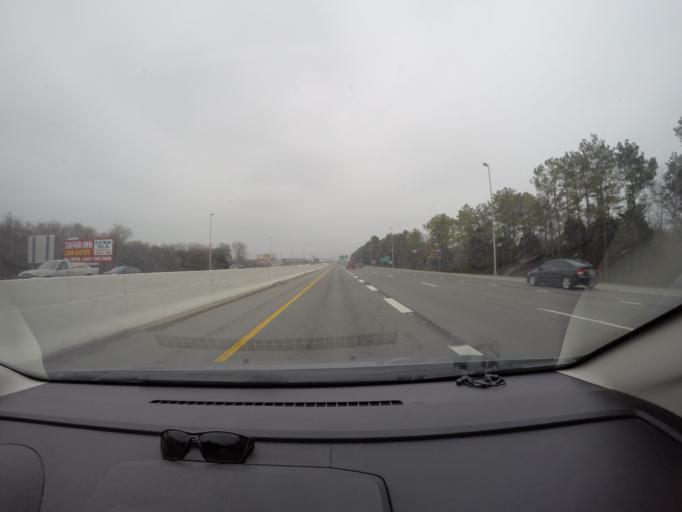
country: US
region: Tennessee
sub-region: Rutherford County
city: Murfreesboro
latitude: 35.8207
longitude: -86.4061
